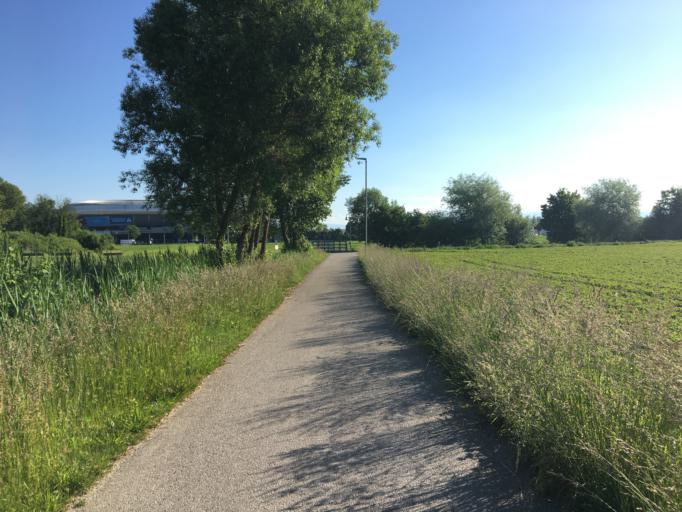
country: AT
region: Carinthia
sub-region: Klagenfurt am Woerthersee
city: Klagenfurt am Woerthersee
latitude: 46.6042
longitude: 14.2771
